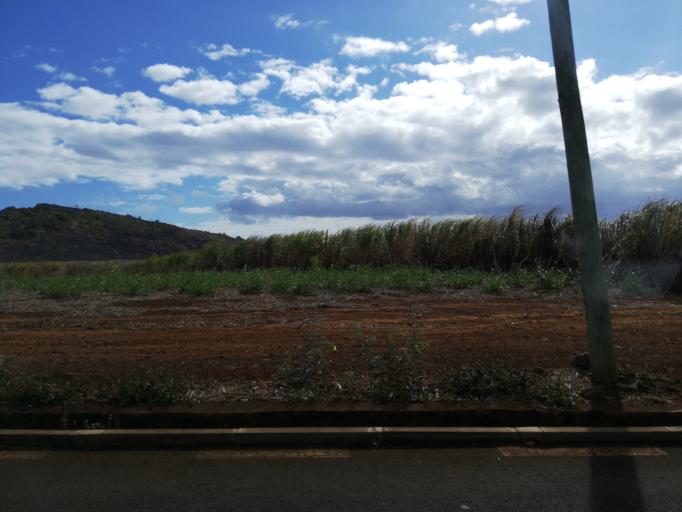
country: MU
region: Black River
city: Gros Cailloux
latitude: -20.2249
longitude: 57.4545
